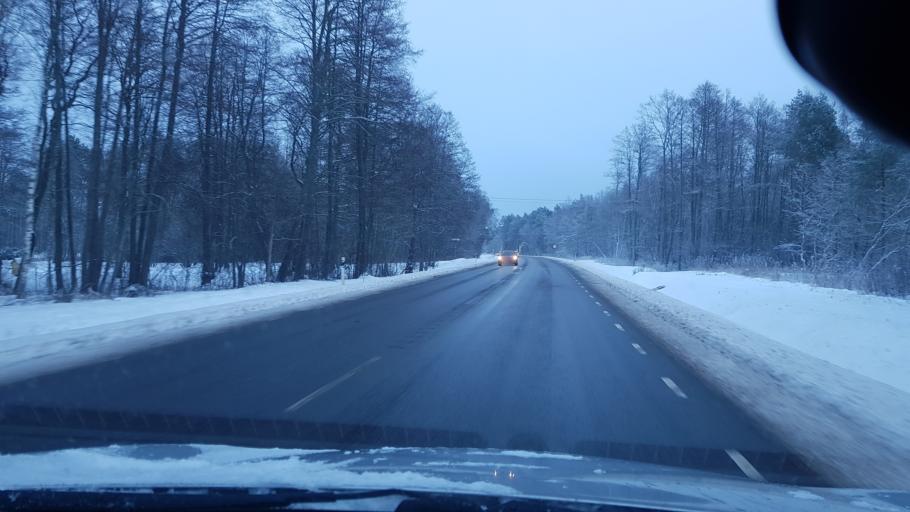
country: EE
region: Harju
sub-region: Keila linn
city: Keila
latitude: 59.3368
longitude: 24.2347
